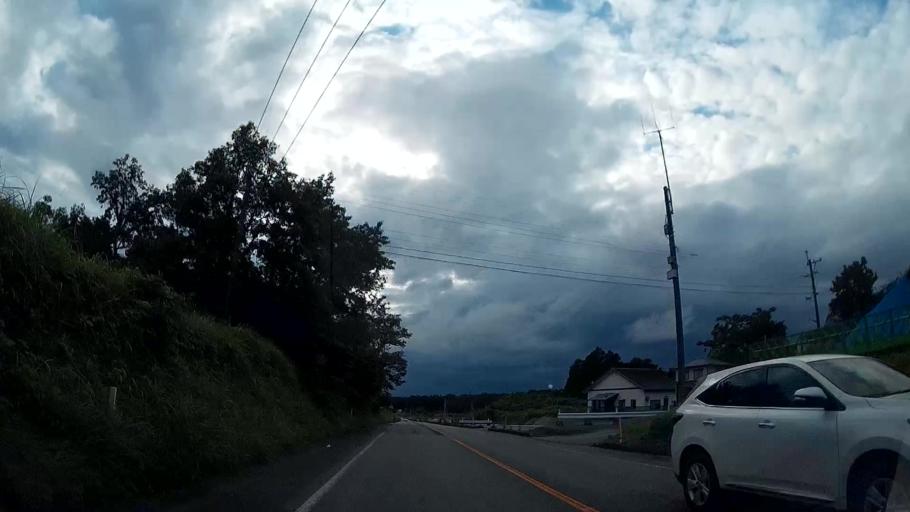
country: JP
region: Kumamoto
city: Ozu
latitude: 32.8781
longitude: 130.9160
